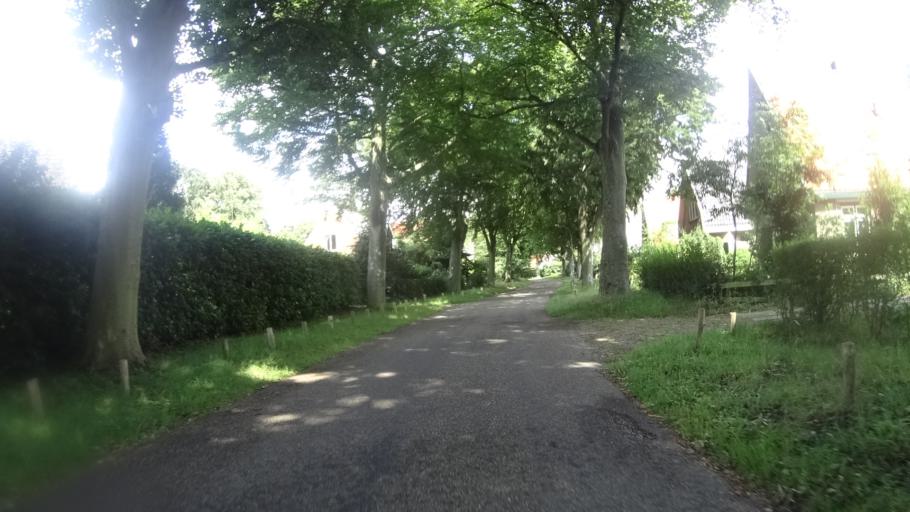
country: NL
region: North Holland
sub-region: Gemeente Schagen
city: Harenkarspel
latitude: 52.7011
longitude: 4.7003
